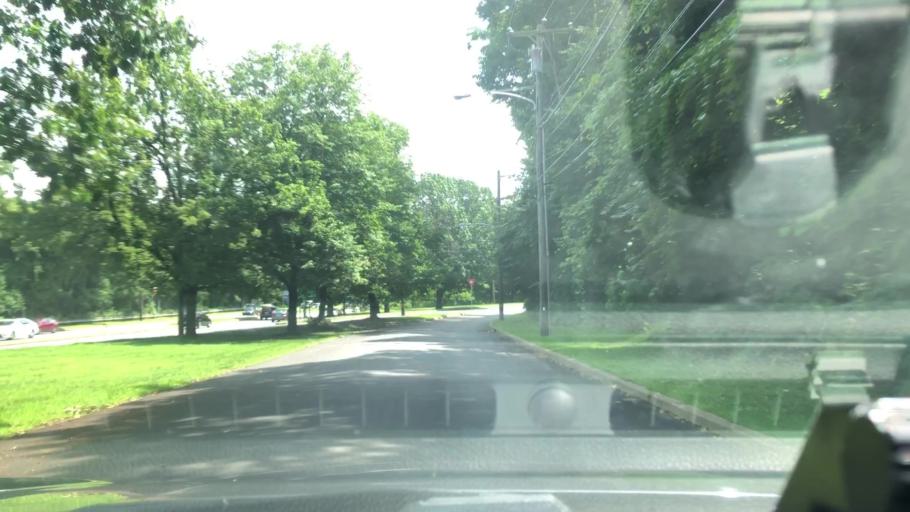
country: US
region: Pennsylvania
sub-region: Montgomery County
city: Flourtown
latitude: 40.0857
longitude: -75.2120
